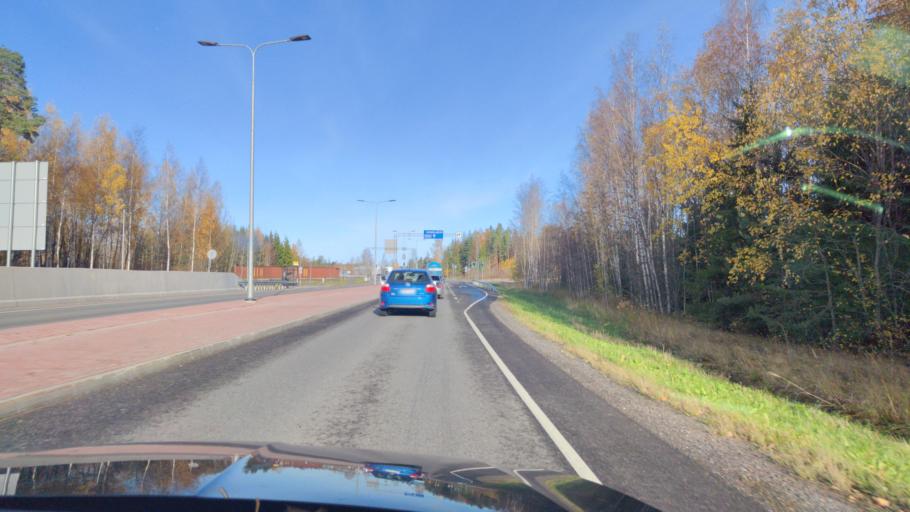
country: FI
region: Varsinais-Suomi
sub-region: Turku
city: Kaarina
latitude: 60.4271
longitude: 22.3818
